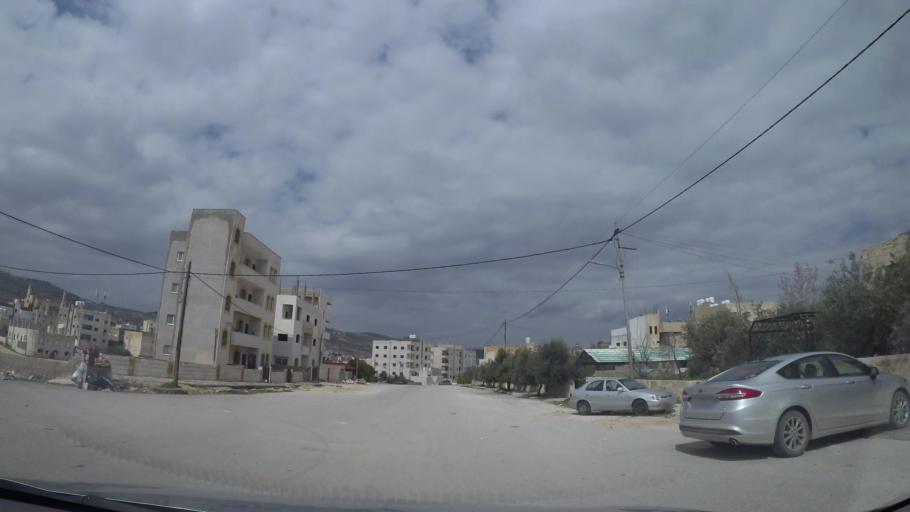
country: JO
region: Amman
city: Al Jubayhah
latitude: 32.0520
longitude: 35.8228
